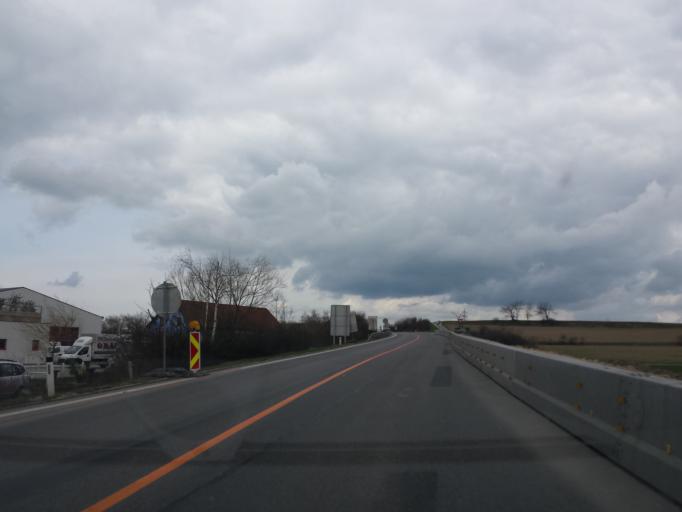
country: AT
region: Lower Austria
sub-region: Politischer Bezirk Krems
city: Gfohl
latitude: 48.5142
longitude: 15.5099
